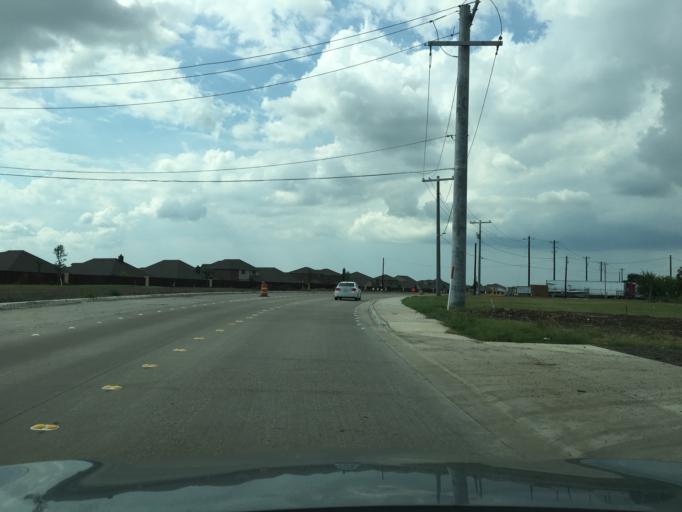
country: US
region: Texas
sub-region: Denton County
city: Oak Point
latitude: 33.1973
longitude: -96.9782
